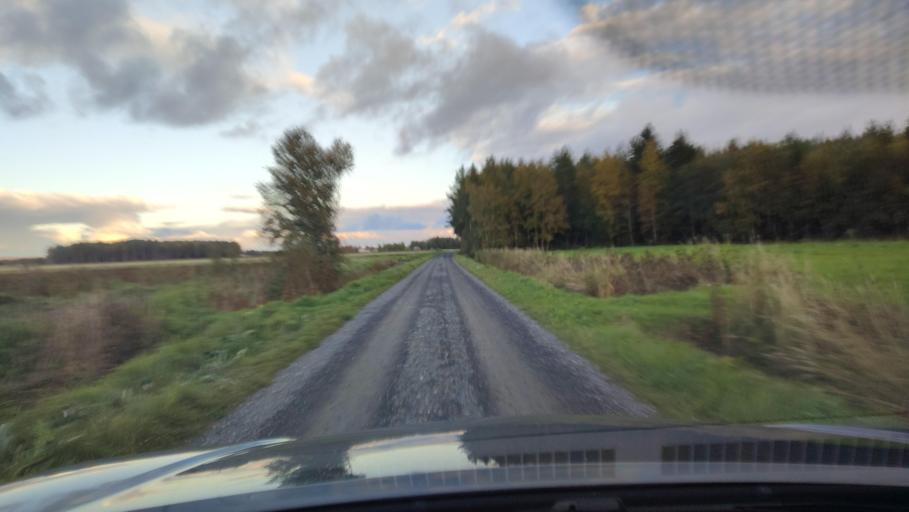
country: FI
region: Ostrobothnia
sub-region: Sydosterbotten
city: Kristinestad
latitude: 62.2508
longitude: 21.4621
